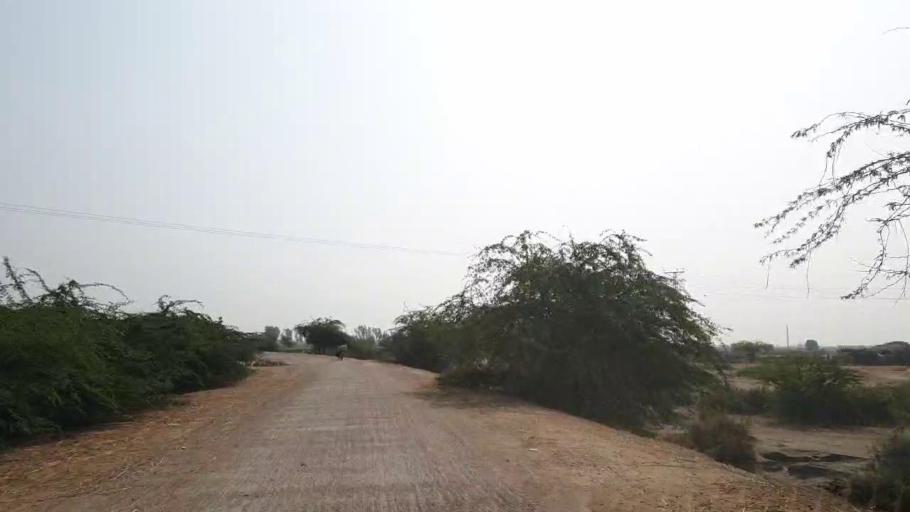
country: PK
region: Sindh
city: Matli
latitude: 24.9990
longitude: 68.5734
